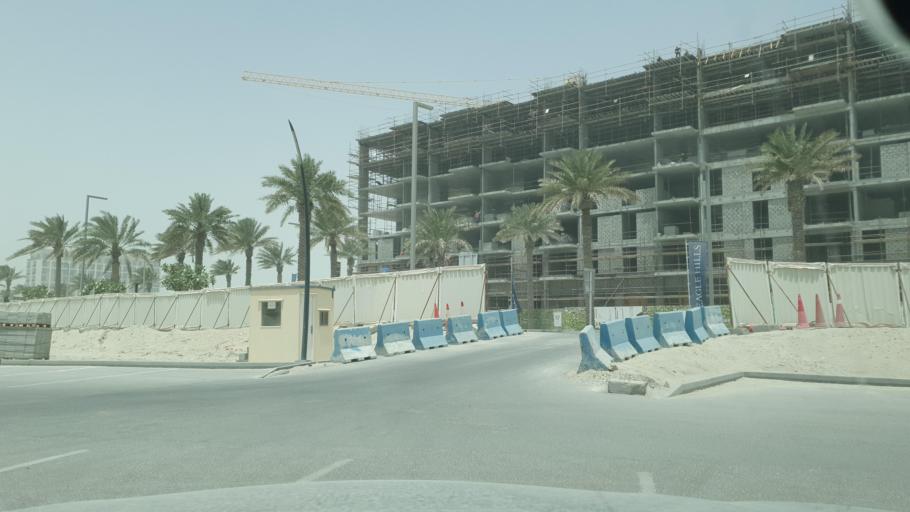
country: BH
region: Muharraq
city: Al Muharraq
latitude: 26.3070
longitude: 50.6469
